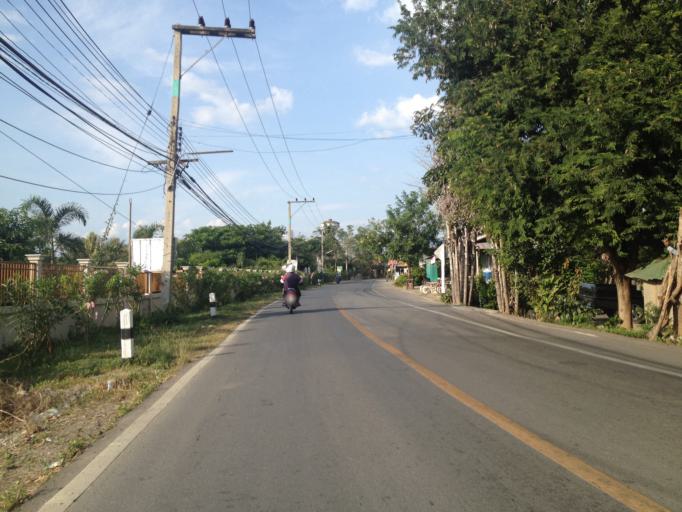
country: TH
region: Chiang Mai
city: Saraphi
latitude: 18.6849
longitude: 98.9851
